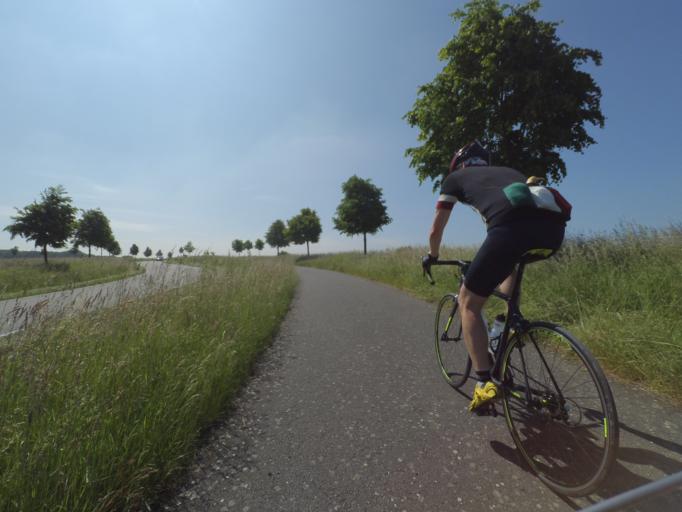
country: DE
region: Rheinland-Pfalz
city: Nortershausen
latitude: 50.2039
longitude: 7.4994
